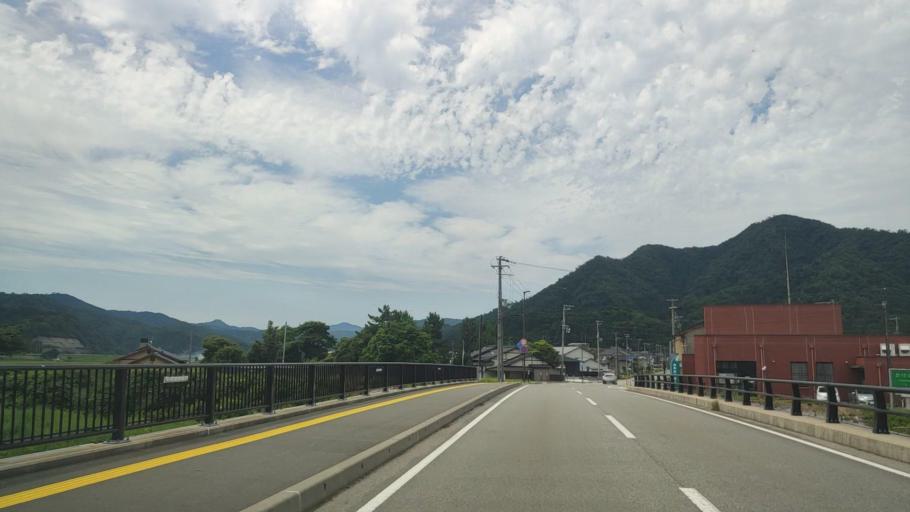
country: JP
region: Hyogo
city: Toyooka
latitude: 35.6540
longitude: 134.7605
